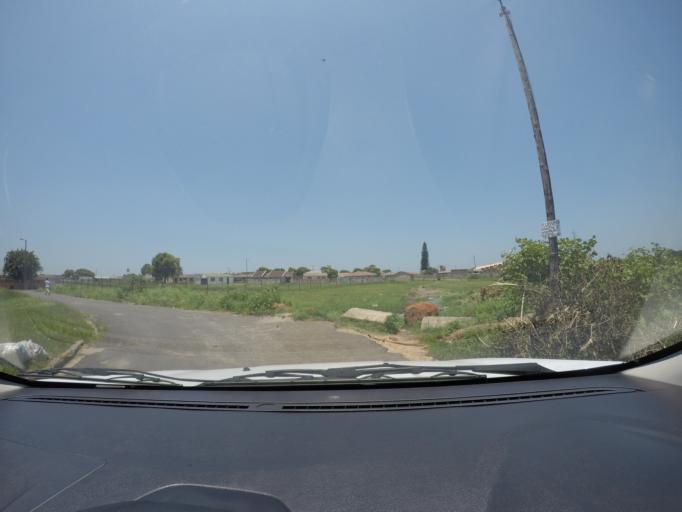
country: ZA
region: KwaZulu-Natal
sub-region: uThungulu District Municipality
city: eSikhawini
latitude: -28.8818
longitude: 31.8994
